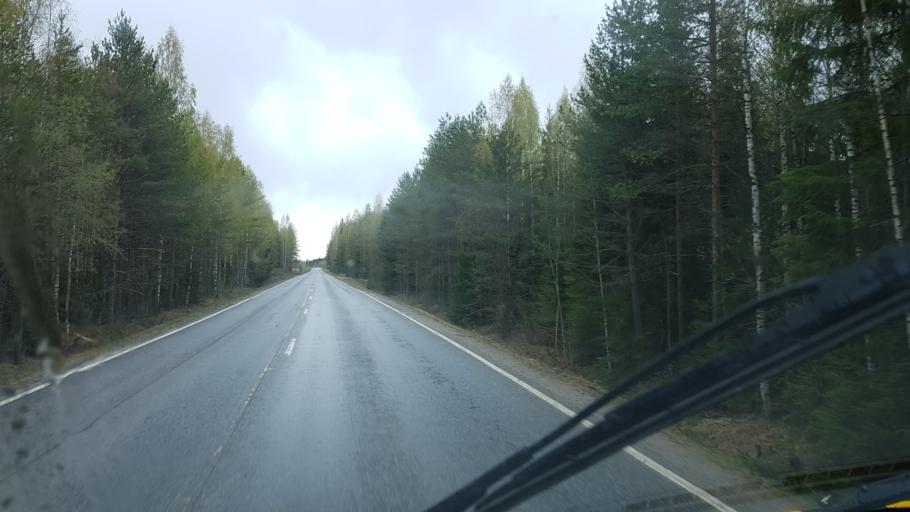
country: FI
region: Pirkanmaa
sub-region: Tampere
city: Pirkkala
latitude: 61.3981
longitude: 23.6283
